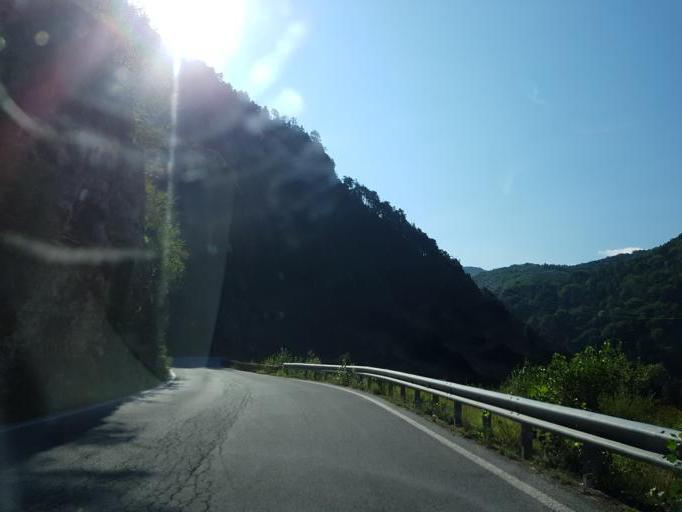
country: IT
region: Piedmont
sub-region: Provincia di Cuneo
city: Macra
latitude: 44.4962
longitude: 7.2021
